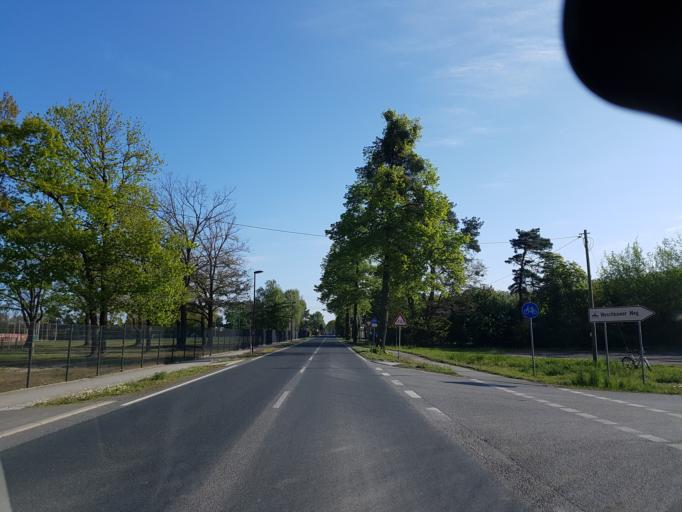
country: DE
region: Brandenburg
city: Grossraschen
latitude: 51.5928
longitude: 14.0128
